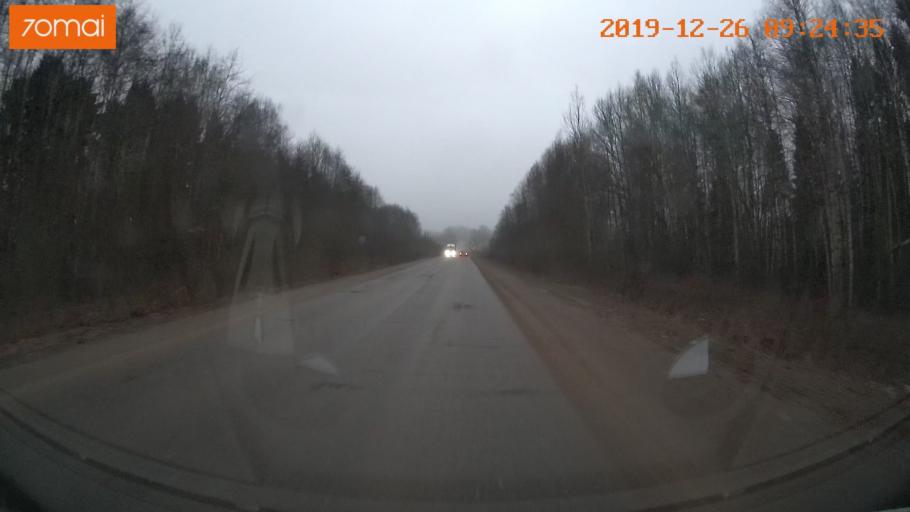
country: RU
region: Vologda
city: Gryazovets
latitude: 59.0024
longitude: 40.1971
